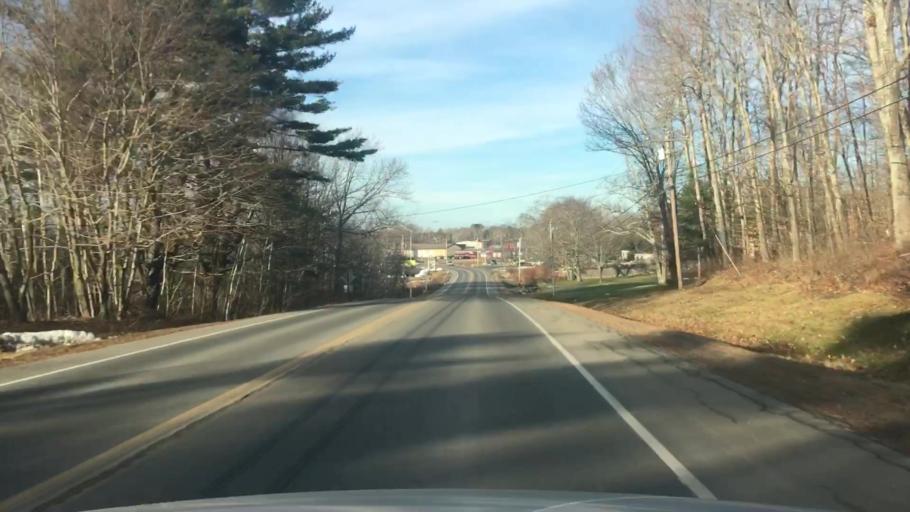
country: US
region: Maine
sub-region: Lincoln County
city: Wiscasset
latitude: 44.0343
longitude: -69.6728
